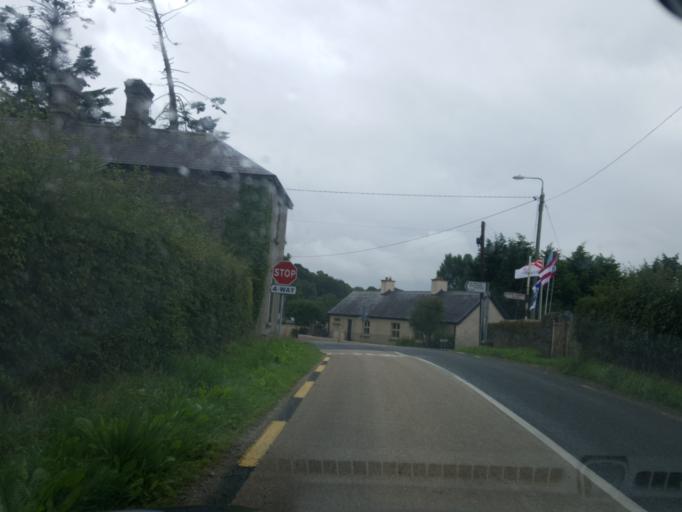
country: IE
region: Leinster
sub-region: Kildare
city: Kilcullen
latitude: 53.1200
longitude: -6.7295
